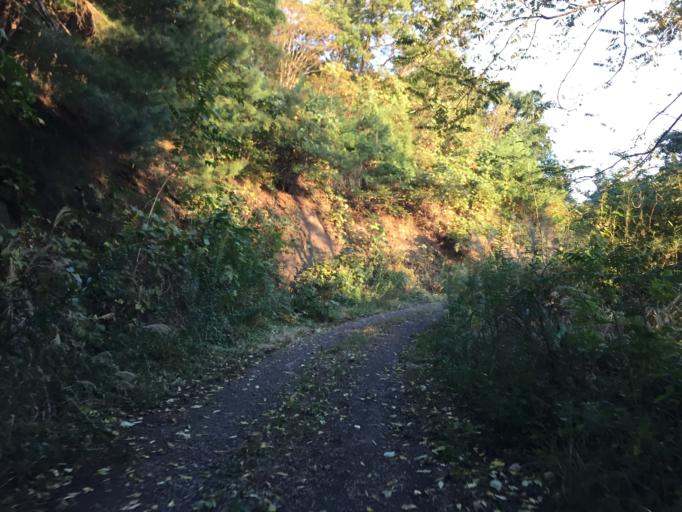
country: JP
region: Fukushima
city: Yanagawamachi-saiwaicho
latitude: 37.8386
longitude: 140.6276
